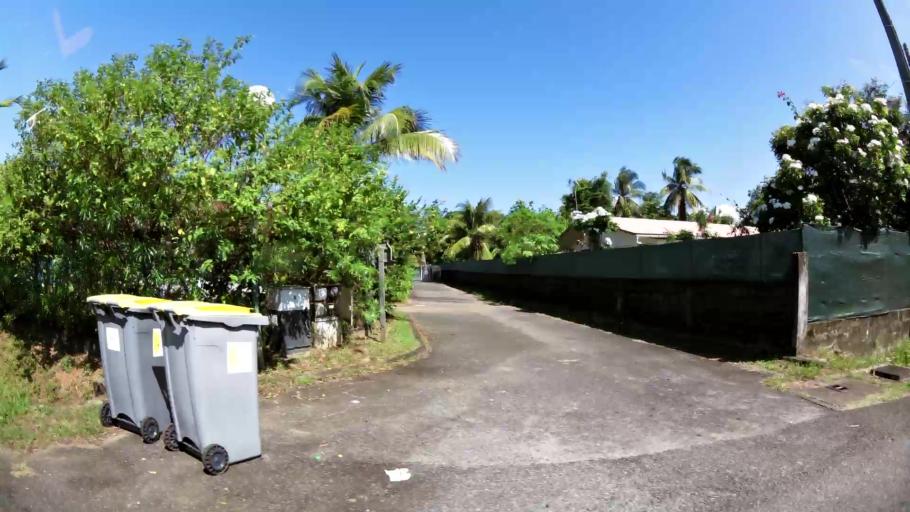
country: GF
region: Guyane
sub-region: Guyane
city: Remire-Montjoly
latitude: 4.9221
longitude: -52.2789
